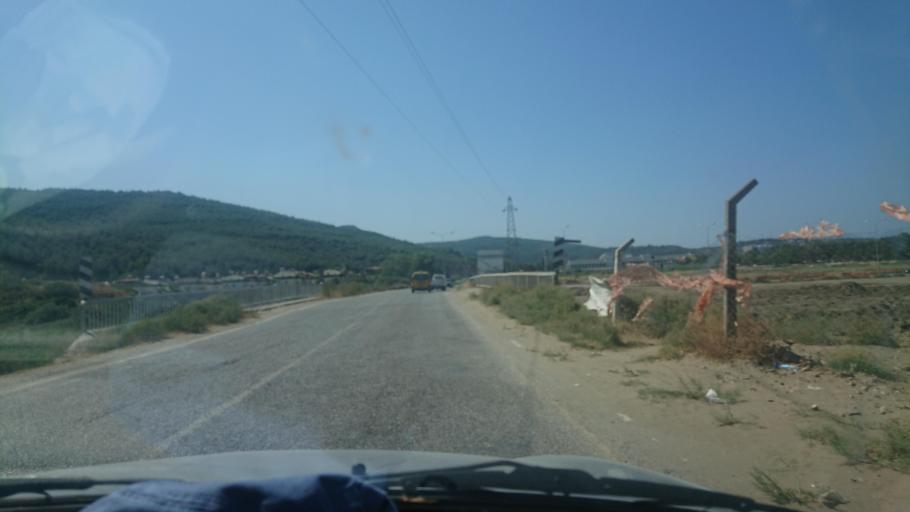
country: TR
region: Izmir
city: Selcuk
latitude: 37.9431
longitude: 27.2799
